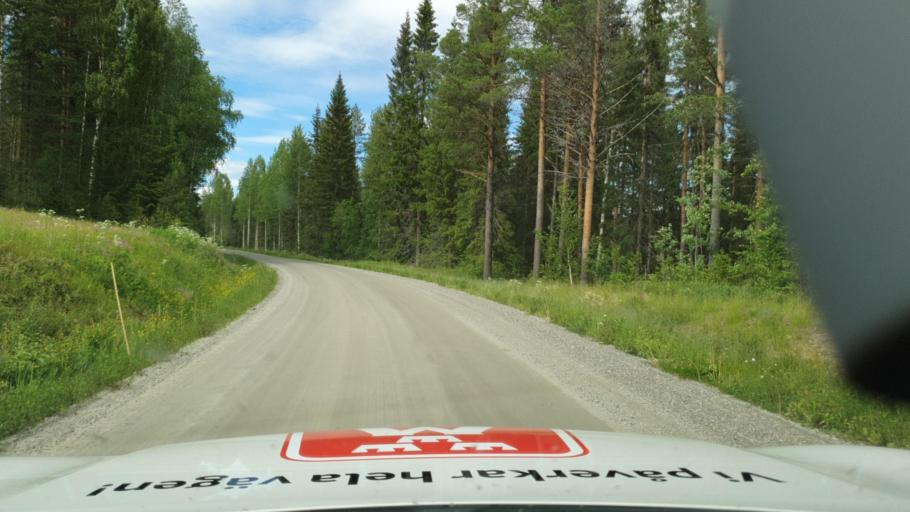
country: SE
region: Vaesterbotten
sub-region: Norsjo Kommun
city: Norsjoe
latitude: 64.8623
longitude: 19.7059
